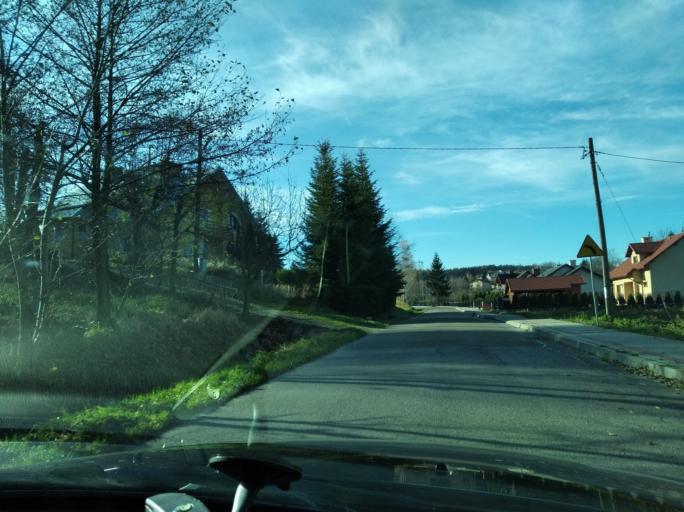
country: PL
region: Subcarpathian Voivodeship
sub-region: Powiat rzeszowski
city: Lutoryz
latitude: 49.9658
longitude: 21.9006
